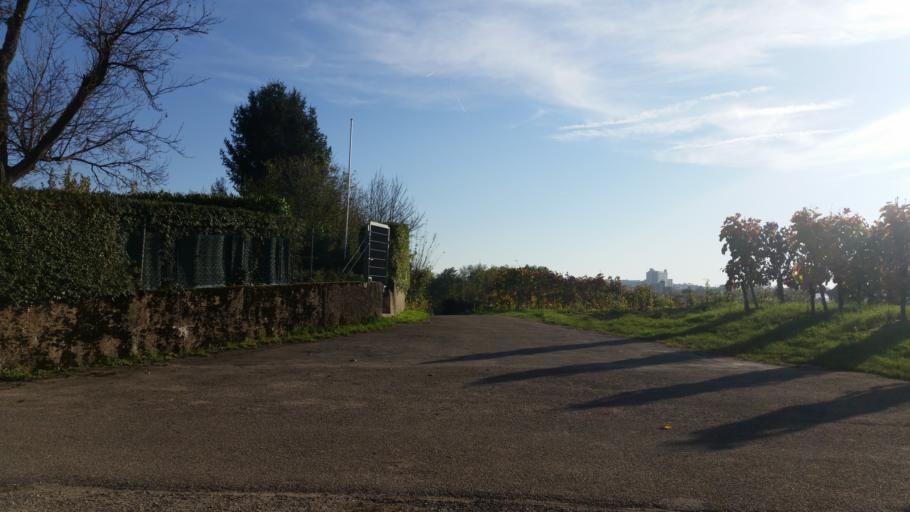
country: DE
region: Baden-Wuerttemberg
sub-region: Regierungsbezirk Stuttgart
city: Freiberg am Neckar
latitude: 48.9155
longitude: 9.2082
